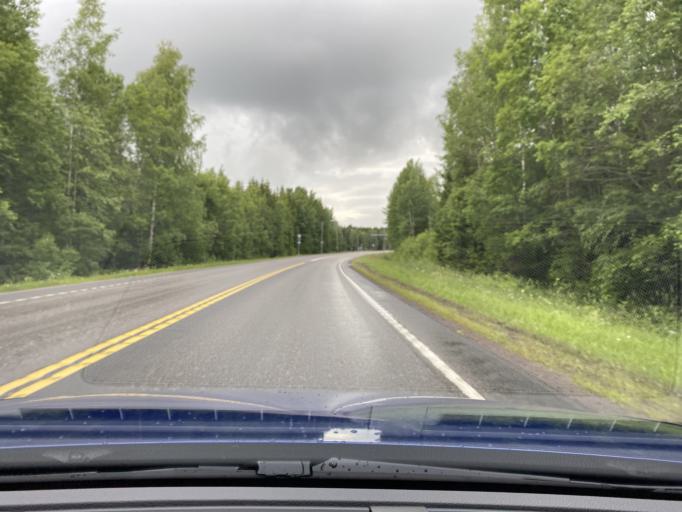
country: FI
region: Uusimaa
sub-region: Helsinki
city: Hyvinge
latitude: 60.5754
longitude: 24.7978
